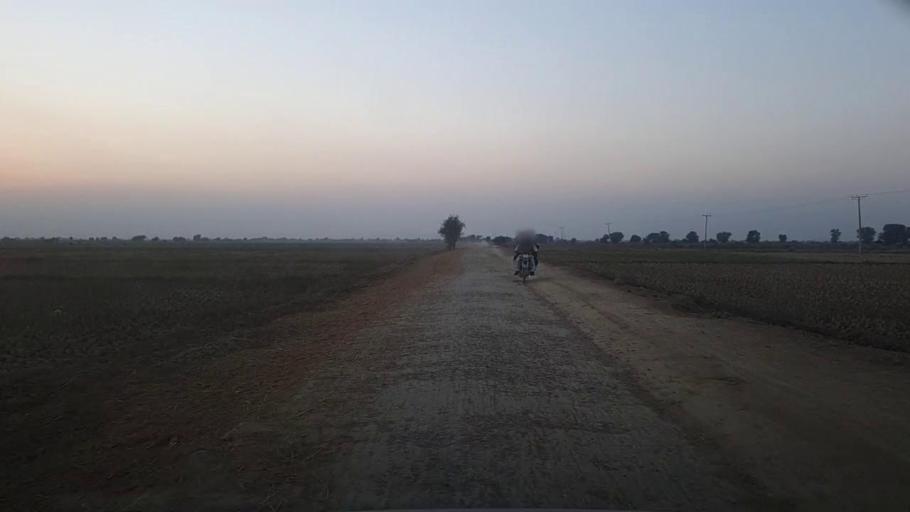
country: PK
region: Sindh
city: Khairpur Nathan Shah
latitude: 27.1803
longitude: 67.6127
